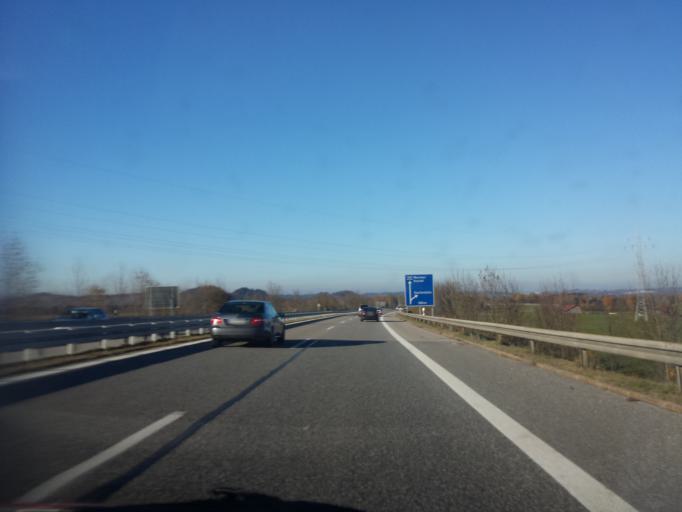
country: DE
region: Bavaria
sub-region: Upper Bavaria
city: Eschenlohe
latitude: 47.5975
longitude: 11.1750
